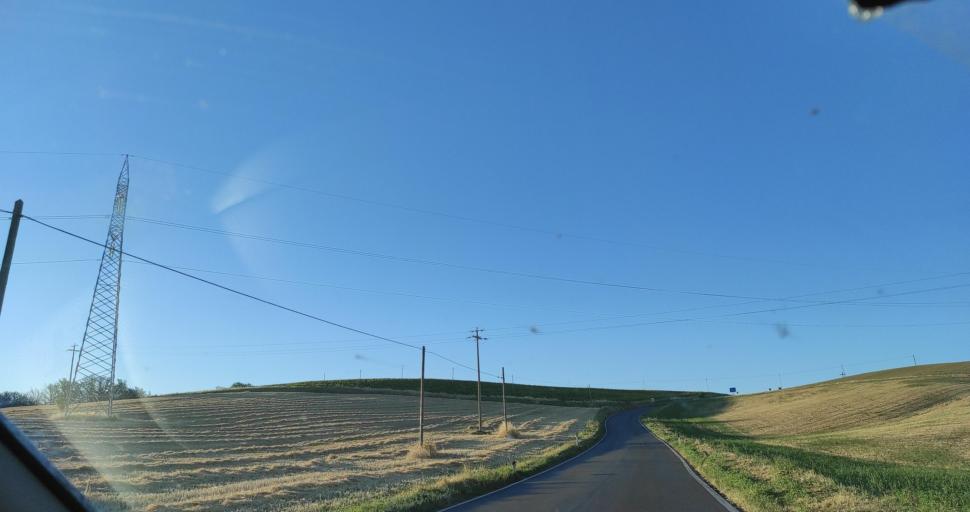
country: IT
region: The Marches
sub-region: Provincia di Macerata
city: Casette Verdini
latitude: 43.2317
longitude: 13.3941
